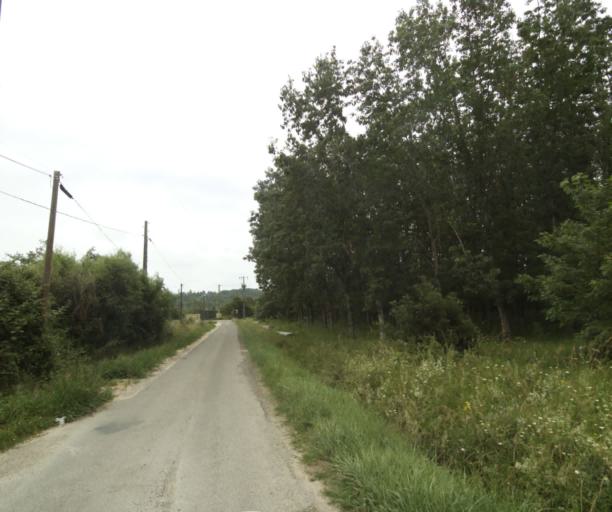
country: FR
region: Midi-Pyrenees
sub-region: Departement du Tarn-et-Garonne
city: Montauban
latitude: 43.9947
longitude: 1.3699
